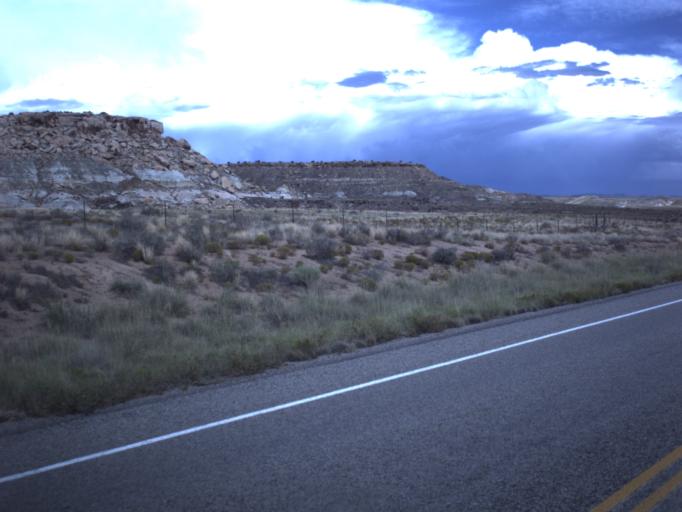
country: US
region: Colorado
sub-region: Montezuma County
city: Towaoc
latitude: 37.1601
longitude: -109.0660
